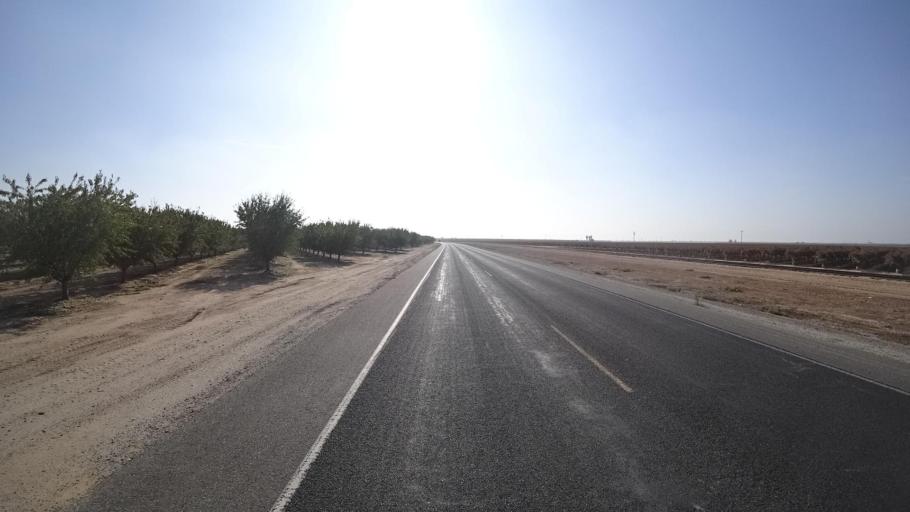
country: US
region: California
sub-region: Kern County
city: McFarland
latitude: 35.6648
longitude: -119.1924
